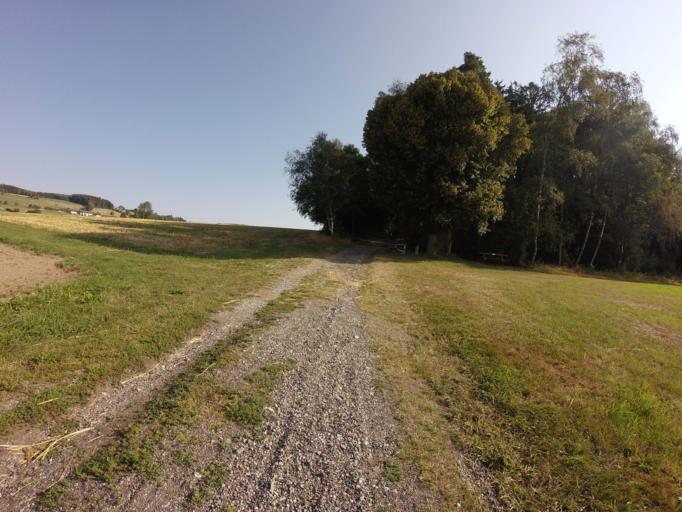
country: AT
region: Upper Austria
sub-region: Politischer Bezirk Urfahr-Umgebung
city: Bad Leonfelden
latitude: 48.5362
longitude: 14.3108
